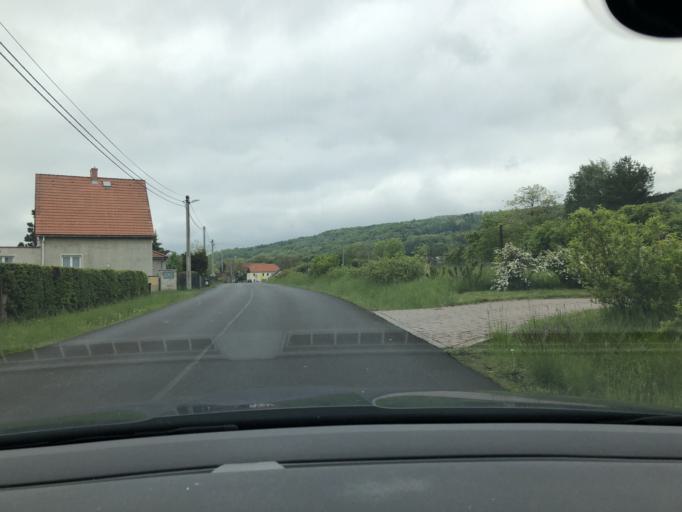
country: CZ
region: Ustecky
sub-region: Okres Usti nad Labem
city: Usti nad Labem
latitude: 50.7031
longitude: 14.0167
